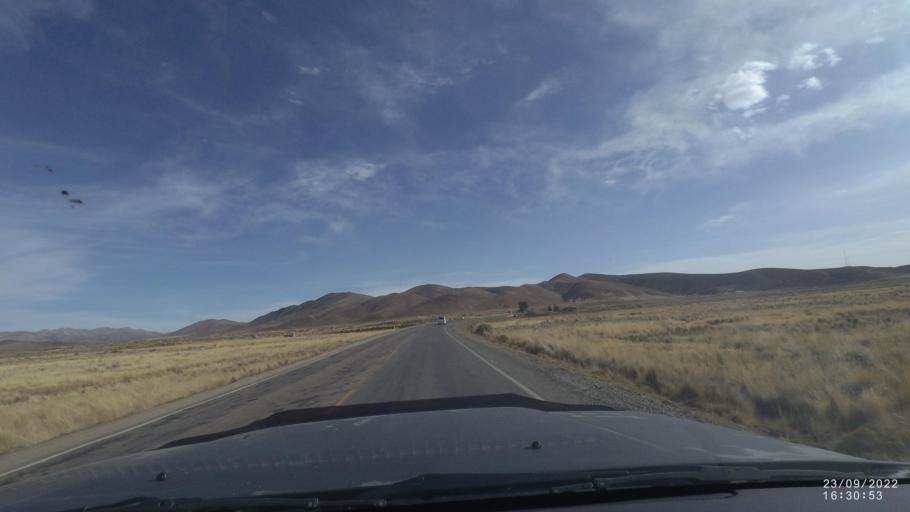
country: BO
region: Oruro
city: Machacamarca
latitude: -18.1603
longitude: -66.9869
